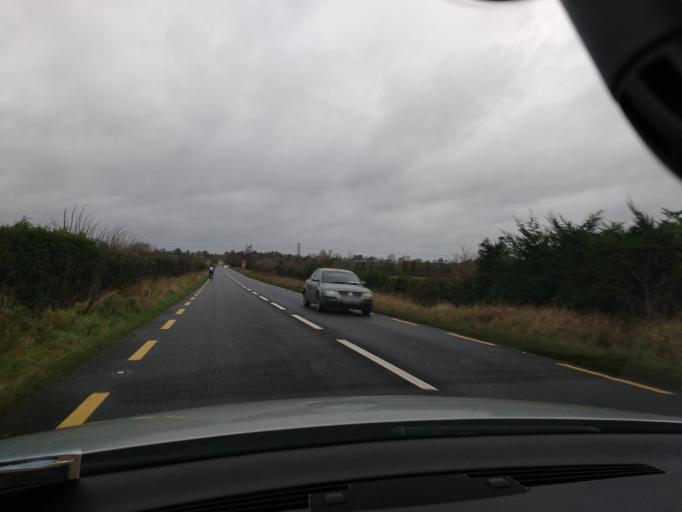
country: IE
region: Munster
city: Thurles
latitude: 52.6753
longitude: -7.7729
